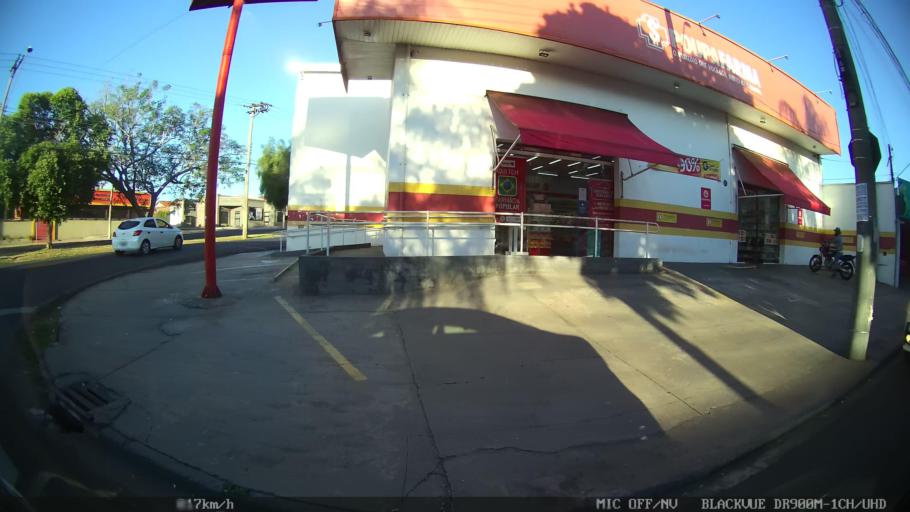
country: BR
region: Sao Paulo
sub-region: Sao Jose Do Rio Preto
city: Sao Jose do Rio Preto
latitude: -20.7787
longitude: -49.3671
